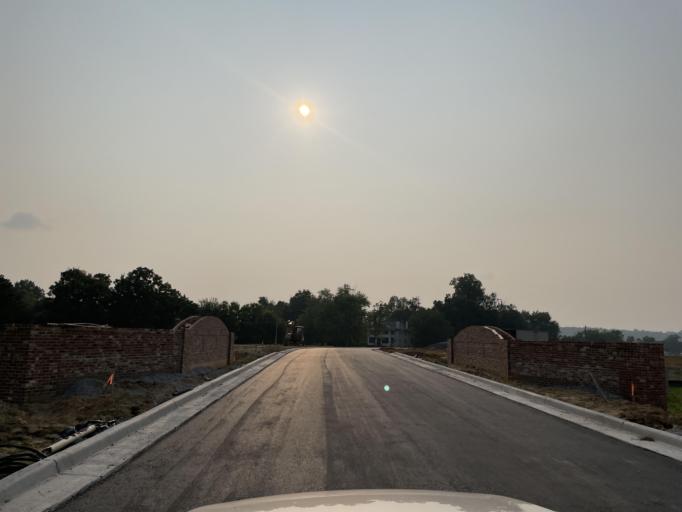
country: US
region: Kentucky
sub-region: Jefferson County
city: Prospect
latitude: 38.3558
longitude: -85.6248
